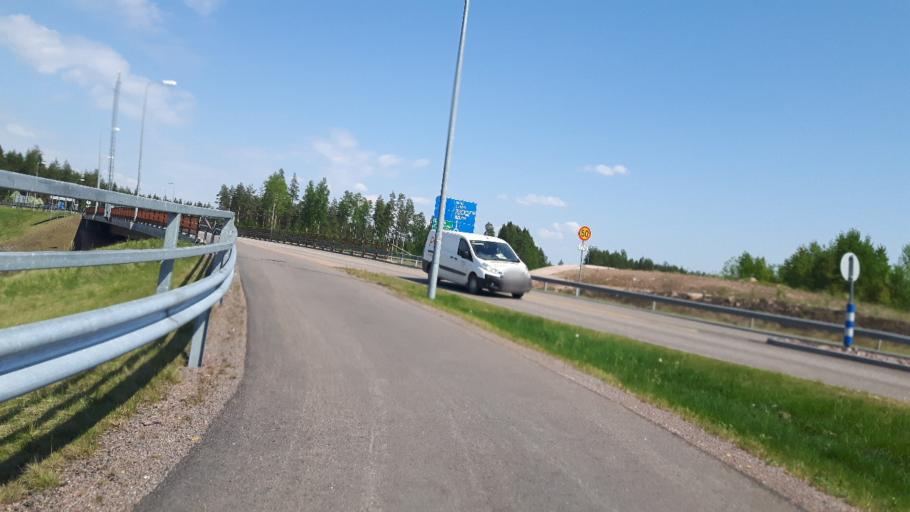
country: FI
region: Uusimaa
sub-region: Loviisa
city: Ruotsinpyhtaeae
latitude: 60.4915
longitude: 26.4185
